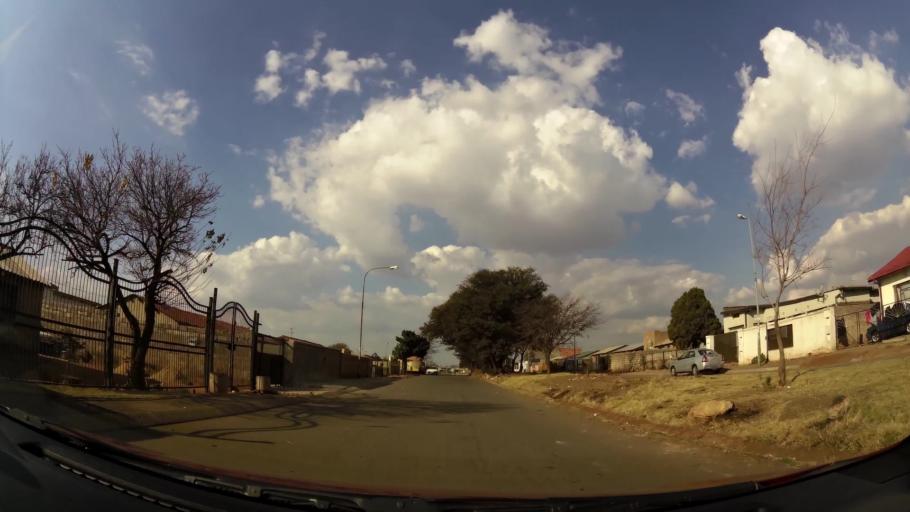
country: ZA
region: Gauteng
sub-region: City of Johannesburg Metropolitan Municipality
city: Soweto
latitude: -26.2287
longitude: 27.8708
